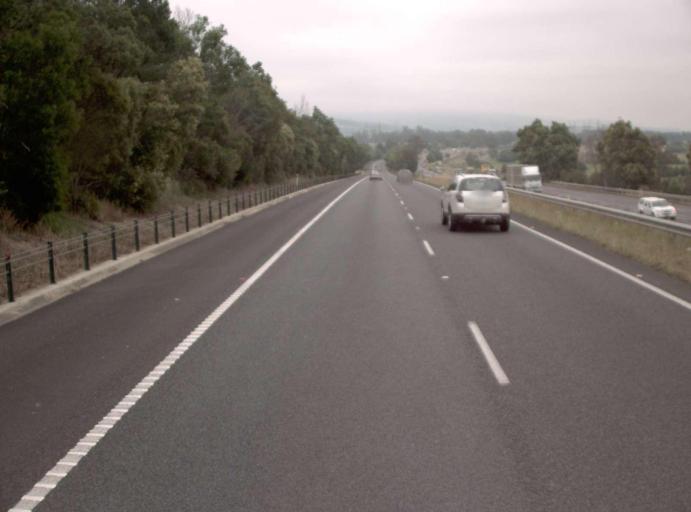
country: AU
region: Victoria
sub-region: Latrobe
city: Moe
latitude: -38.1982
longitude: 146.1980
